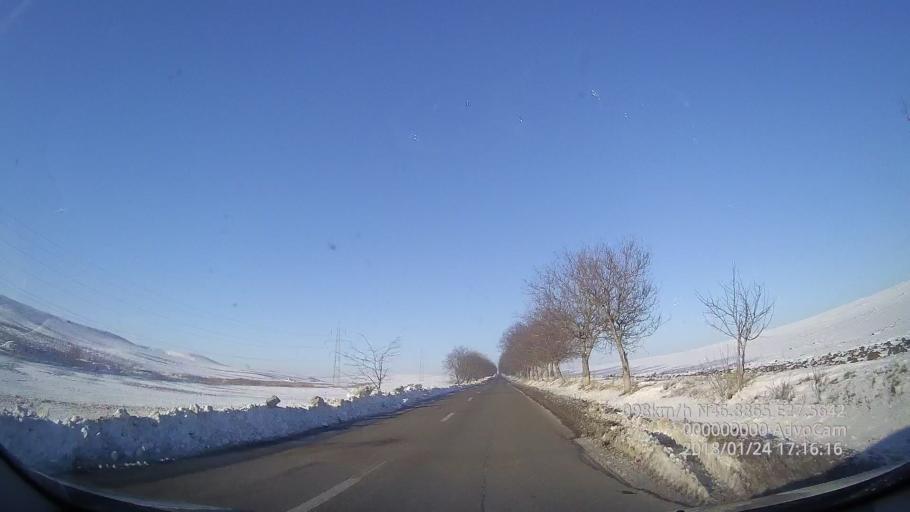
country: RO
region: Vaslui
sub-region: Comuna Rebricea
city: Rebricea
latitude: 46.8873
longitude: 27.5642
